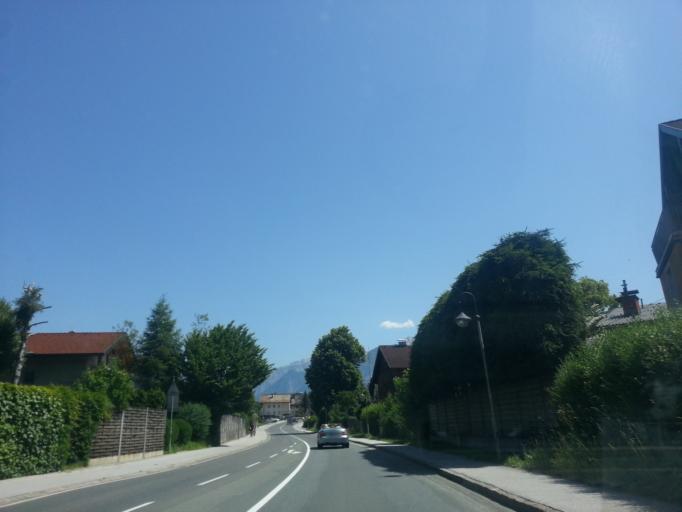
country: AT
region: Salzburg
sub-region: Politischer Bezirk Hallein
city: Kuchl
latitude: 47.6291
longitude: 13.1421
